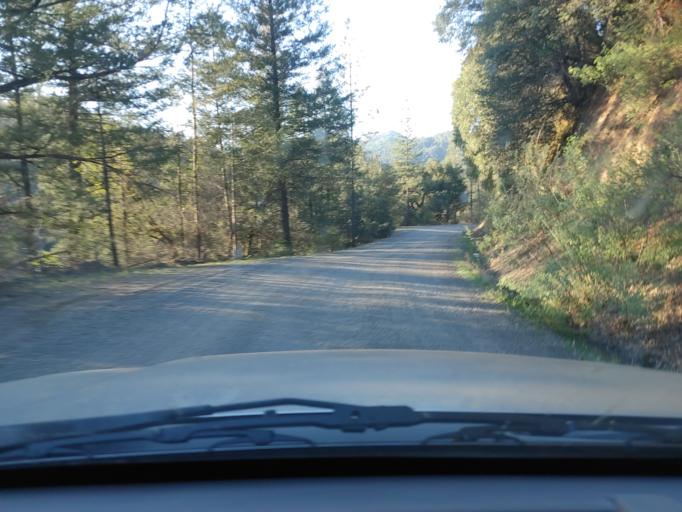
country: US
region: California
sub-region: Shasta County
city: Bella Vista
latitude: 40.8358
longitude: -122.0178
